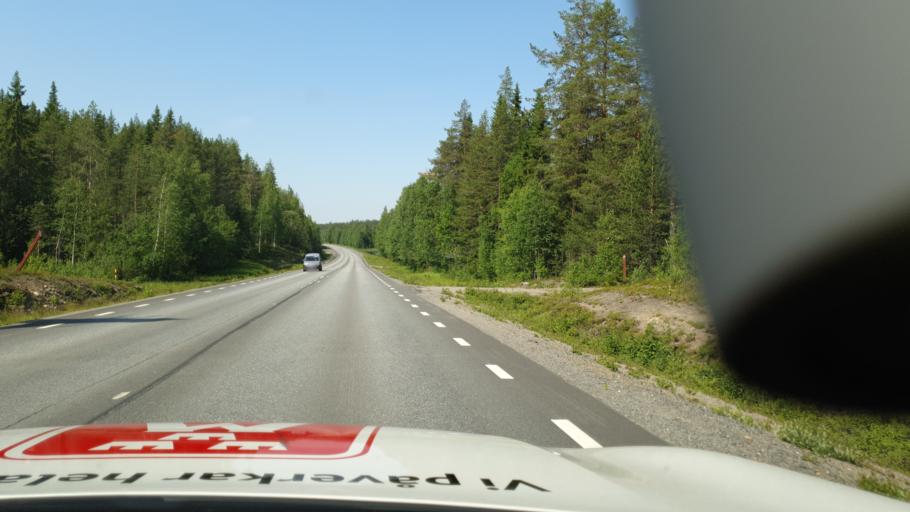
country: SE
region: Vaesterbotten
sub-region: Norsjo Kommun
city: Norsjoe
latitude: 64.9717
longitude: 19.7504
